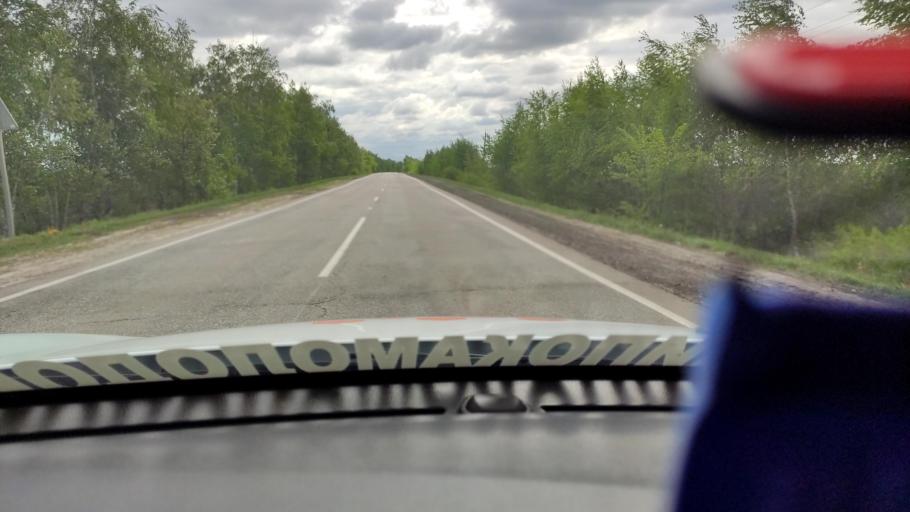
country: RU
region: Voronezj
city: Liski
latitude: 50.7981
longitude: 39.3544
